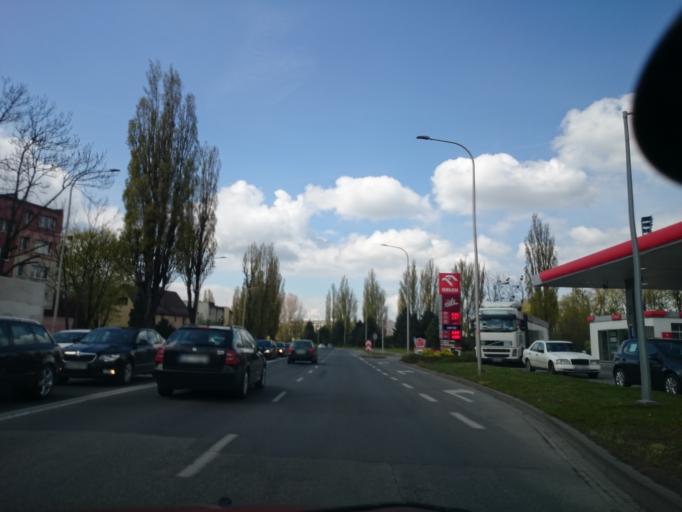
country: PL
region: Opole Voivodeship
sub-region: Powiat opolski
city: Opole
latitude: 50.6745
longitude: 17.9321
